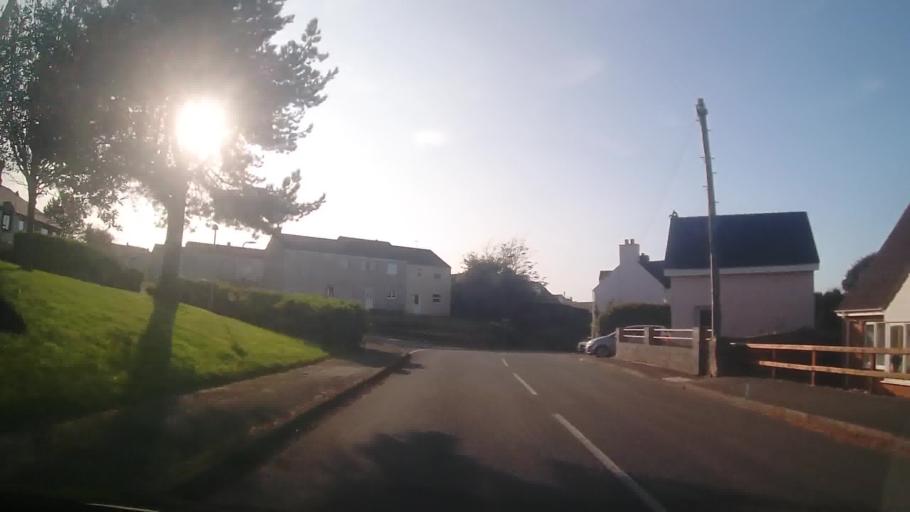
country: GB
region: Wales
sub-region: Pembrokeshire
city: Fishguard
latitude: 51.9918
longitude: -4.9713
